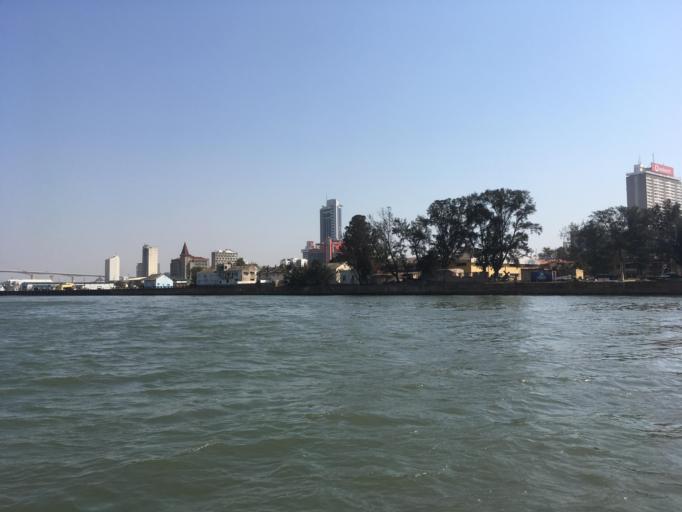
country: MZ
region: Maputo City
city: Maputo
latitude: -25.9797
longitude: 32.5733
